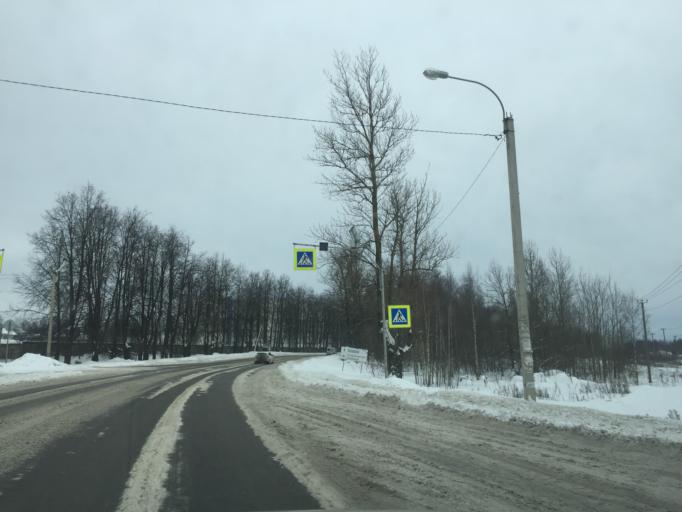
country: RU
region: Leningrad
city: Yanino Vtoroye
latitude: 59.9438
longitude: 30.6041
